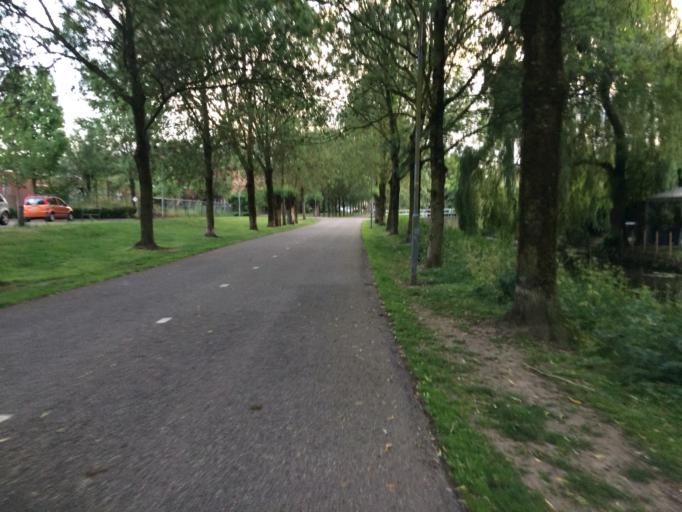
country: NL
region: North Brabant
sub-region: Gemeente 's-Hertogenbosch
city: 's-Hertogenbosch
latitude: 51.7308
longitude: 5.3038
